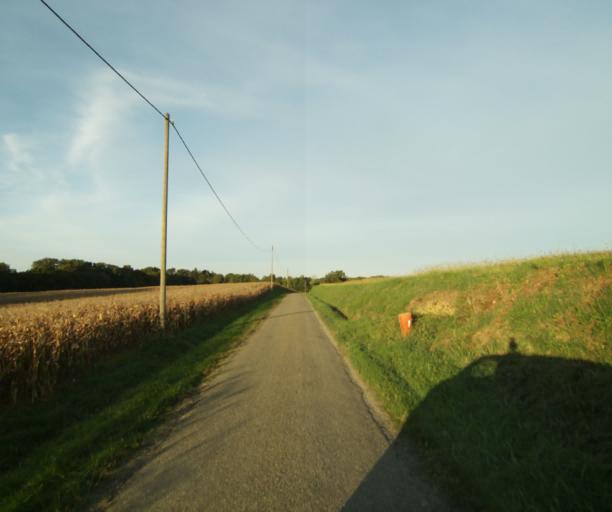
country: FR
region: Midi-Pyrenees
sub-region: Departement du Gers
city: Eauze
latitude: 43.8894
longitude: 0.0509
